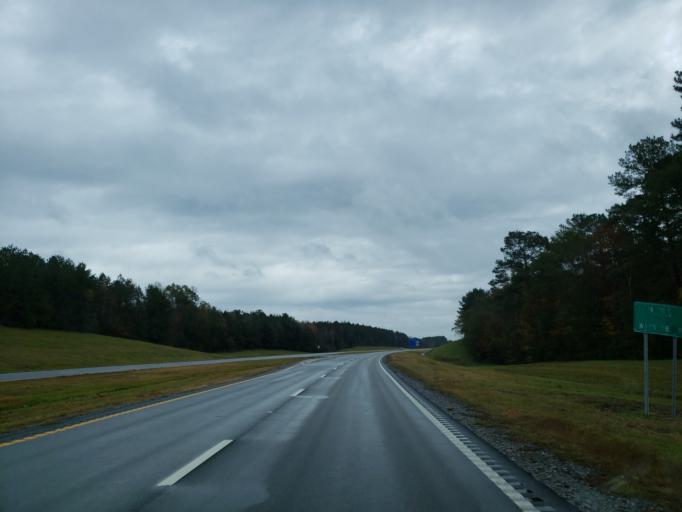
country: US
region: Mississippi
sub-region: Wayne County
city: Waynesboro
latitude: 31.7004
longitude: -88.6552
